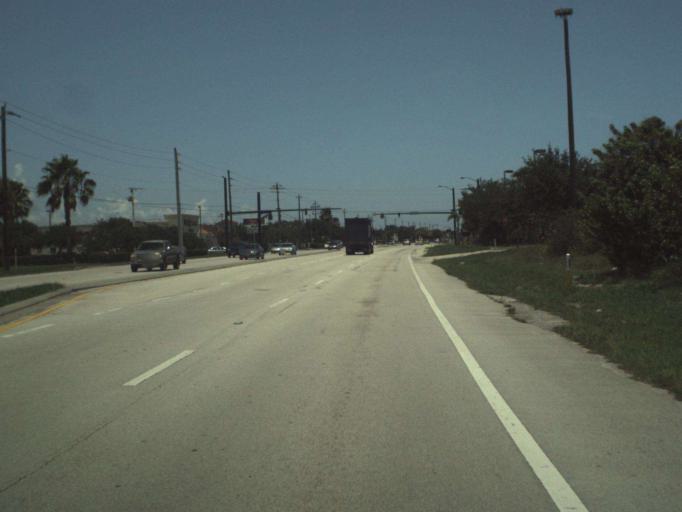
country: US
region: Florida
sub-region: Indian River County
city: Roseland
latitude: 27.8396
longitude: -80.4861
